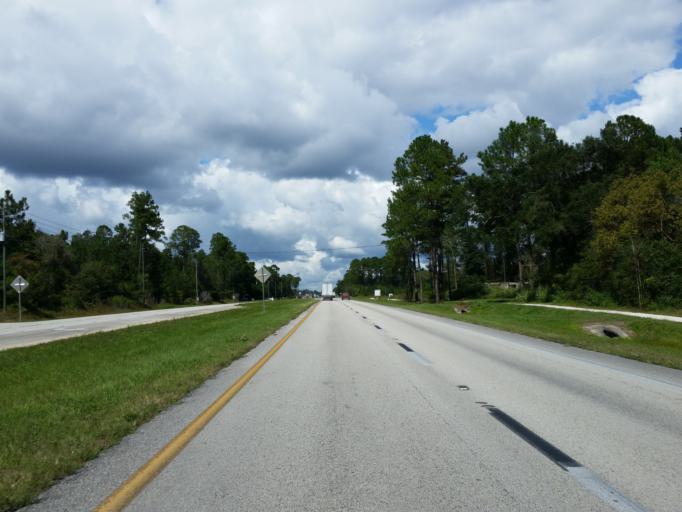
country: US
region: Florida
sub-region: Alachua County
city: Waldo
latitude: 29.8044
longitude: -82.1676
